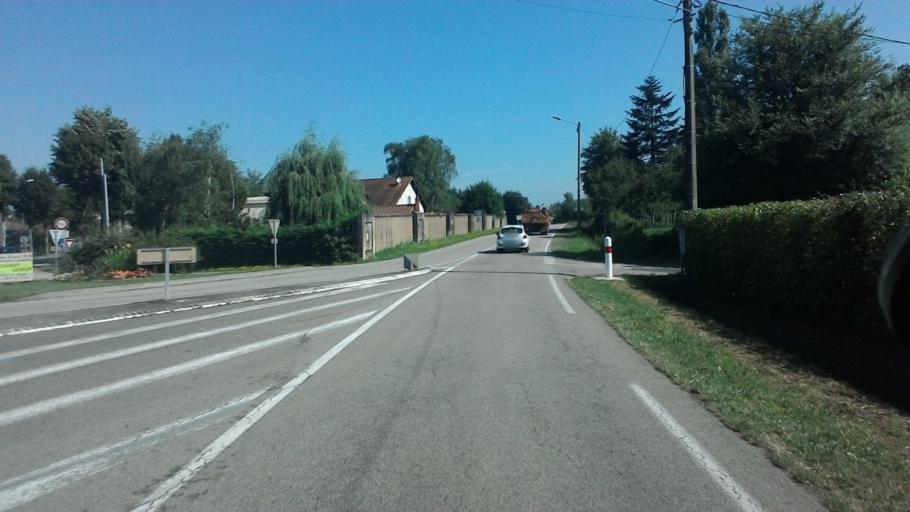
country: FR
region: Rhone-Alpes
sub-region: Departement de l'Ain
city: Saint-Trivier-de-Courtes
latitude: 46.4558
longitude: 5.0844
